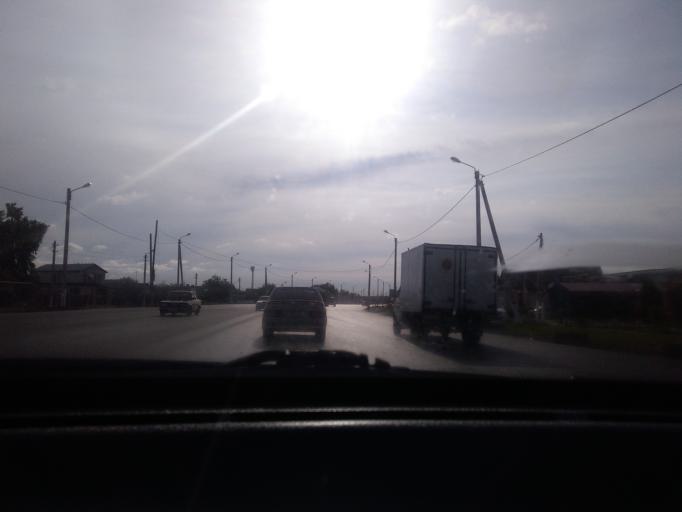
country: RU
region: Kursk
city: Voroshnevo
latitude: 51.6546
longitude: 36.0065
